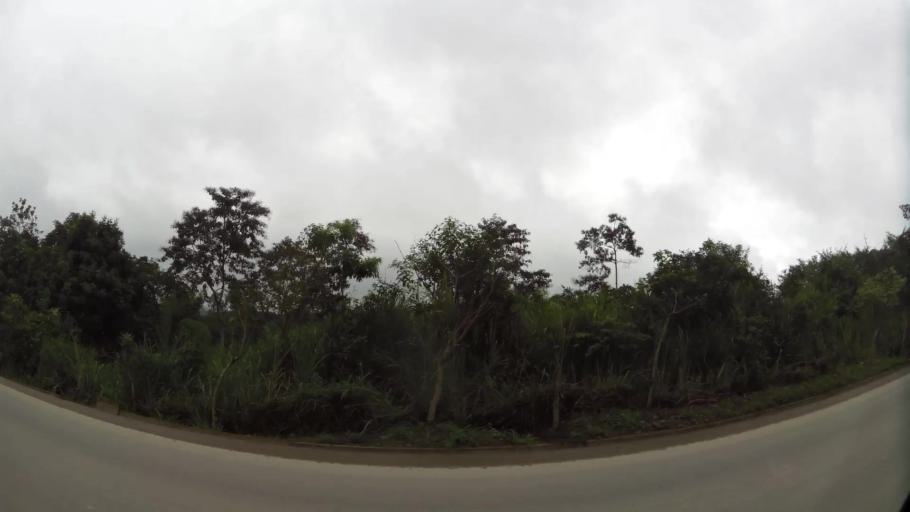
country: EC
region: El Oro
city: Pasaje
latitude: -3.3291
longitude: -79.7635
